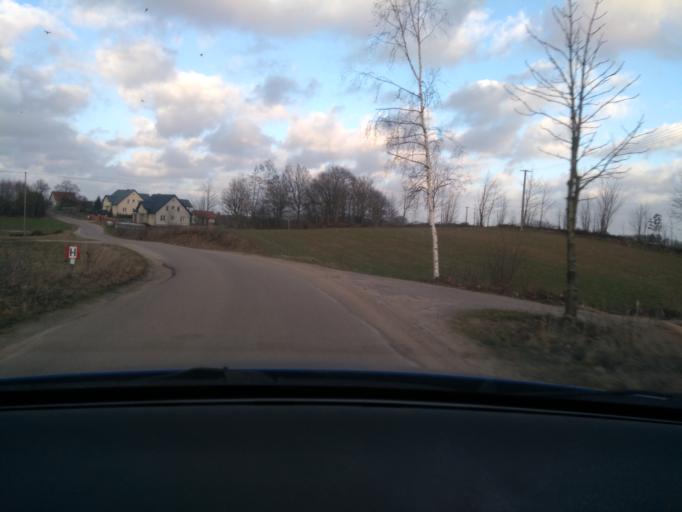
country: PL
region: Pomeranian Voivodeship
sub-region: Powiat kartuski
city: Przodkowo
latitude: 54.4044
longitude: 18.2296
